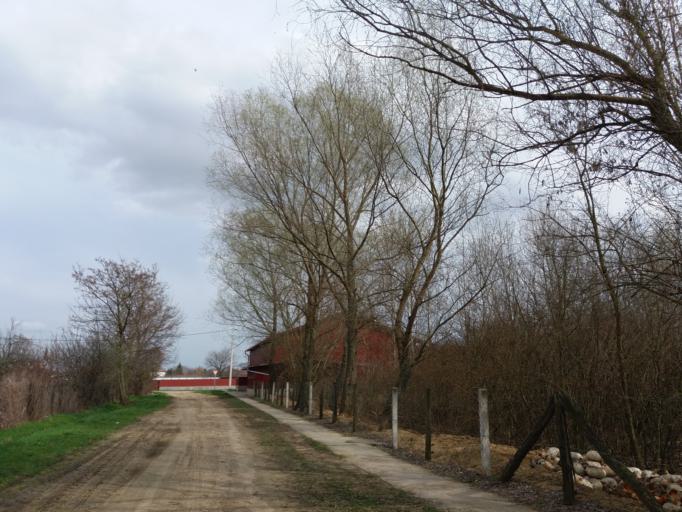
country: HU
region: Szabolcs-Szatmar-Bereg
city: Petnehaza
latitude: 48.0552
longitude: 22.0379
